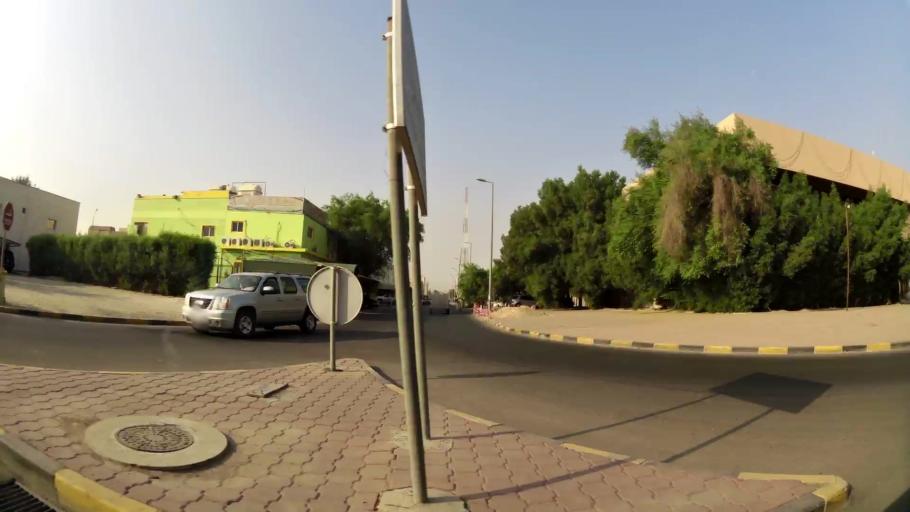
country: KW
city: Bayan
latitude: 29.2998
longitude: 48.0569
